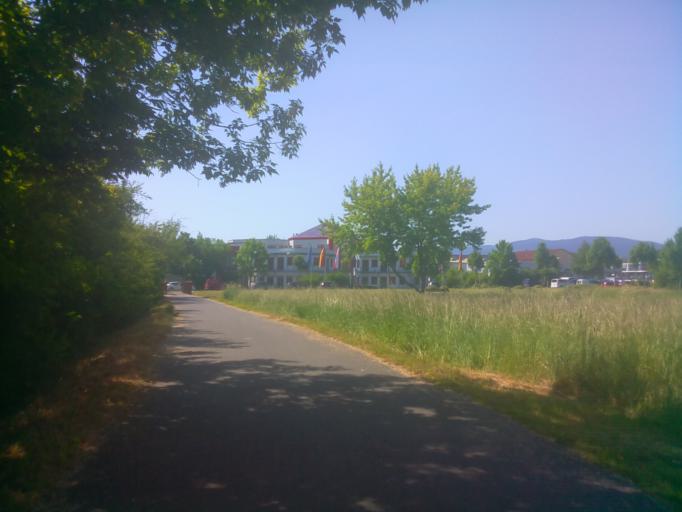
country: DE
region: Thuringia
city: Rudolstadt
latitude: 50.7013
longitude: 11.3298
